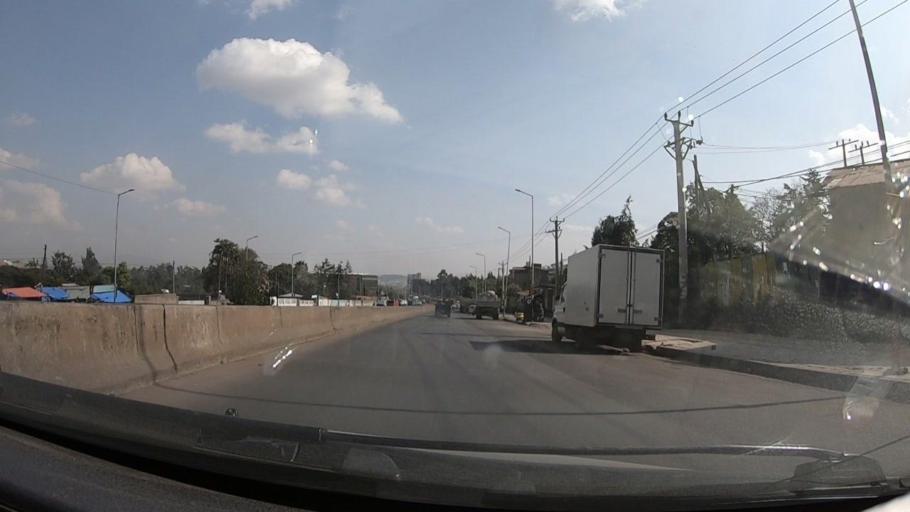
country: ET
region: Adis Abeba
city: Addis Ababa
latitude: 8.9875
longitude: 38.6931
